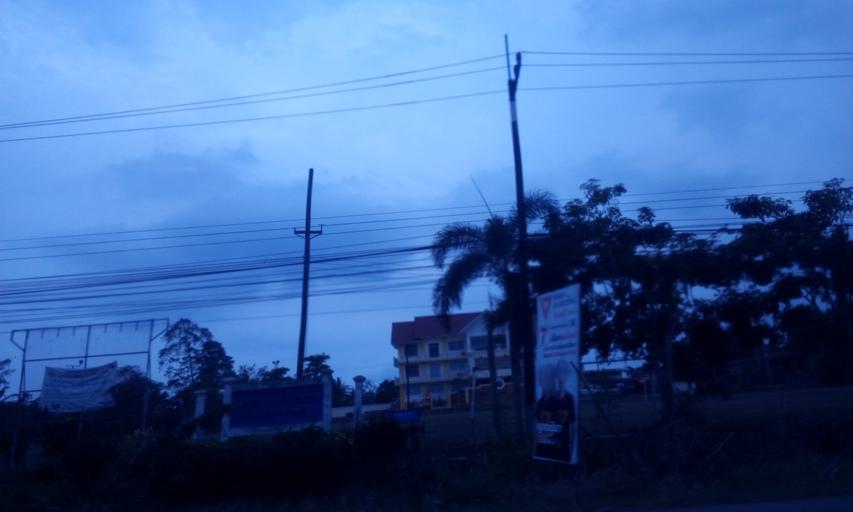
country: TH
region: Chanthaburi
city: Khlung
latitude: 12.4205
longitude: 102.3238
